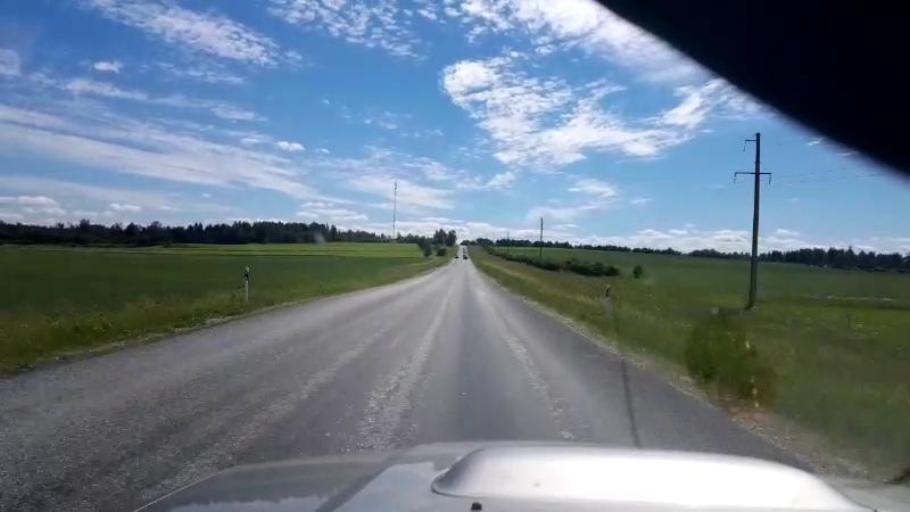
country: EE
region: Laeaene-Virumaa
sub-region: Rakke vald
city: Rakke
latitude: 58.8571
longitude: 26.2926
